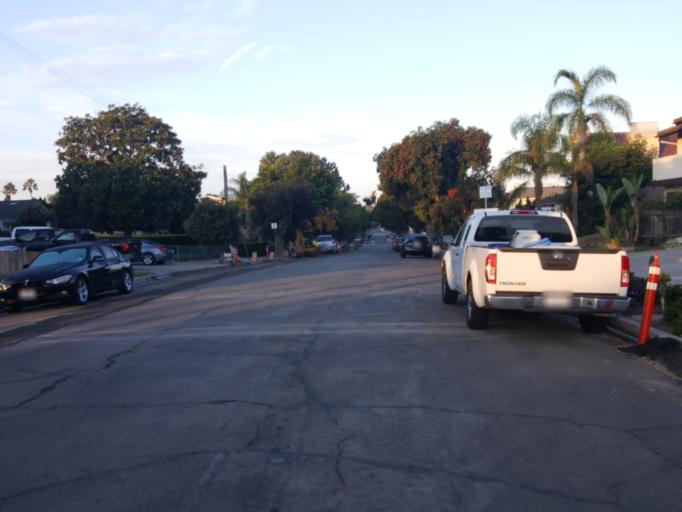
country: US
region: California
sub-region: San Diego County
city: La Jolla
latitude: 32.7985
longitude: -117.2425
